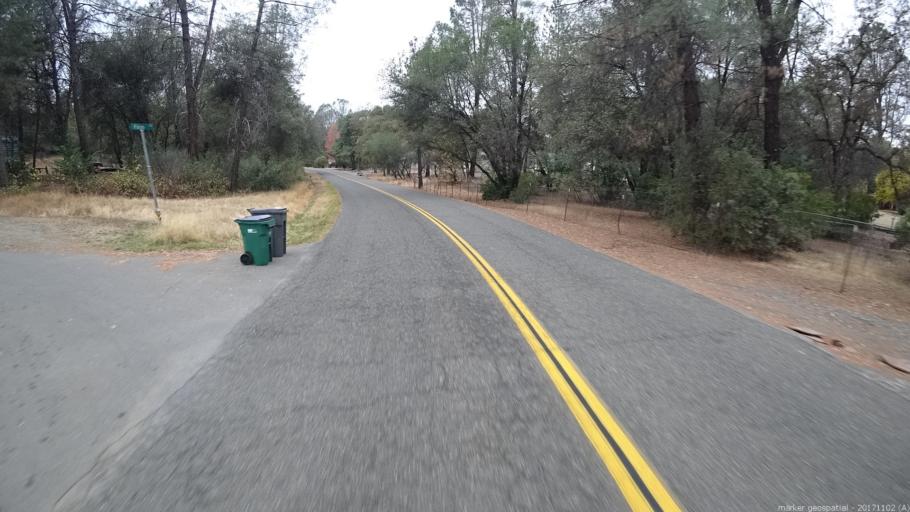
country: US
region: California
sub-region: Shasta County
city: Central Valley (historical)
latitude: 40.6648
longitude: -122.4034
